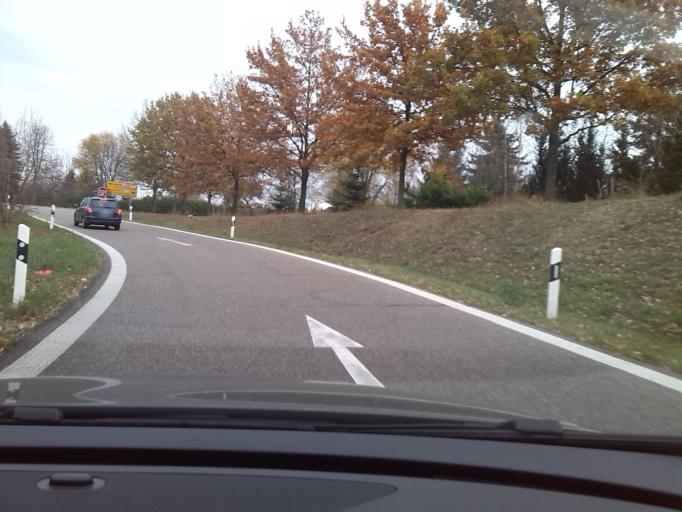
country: DE
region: Baden-Wuerttemberg
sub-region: Regierungsbezirk Stuttgart
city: Fellbach
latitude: 48.8047
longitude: 9.2916
